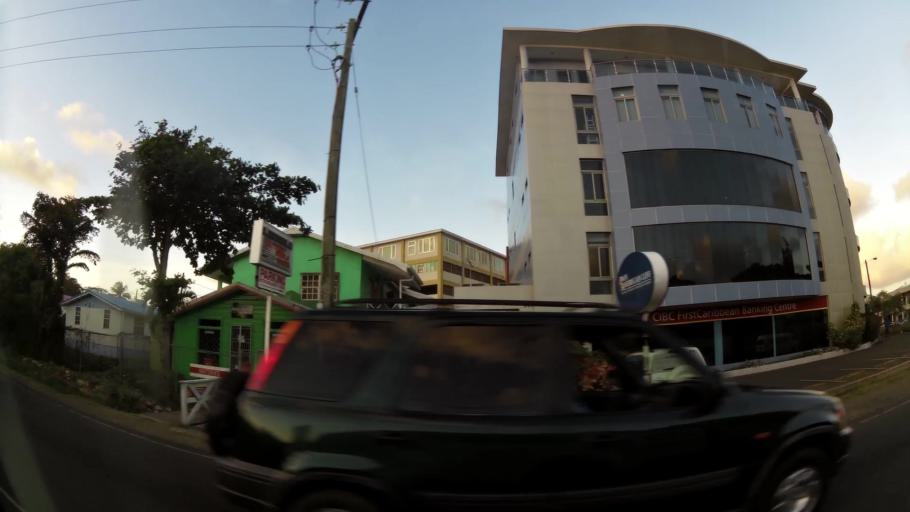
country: LC
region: Gros-Islet
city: Gros Islet
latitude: 14.0679
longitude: -60.9548
